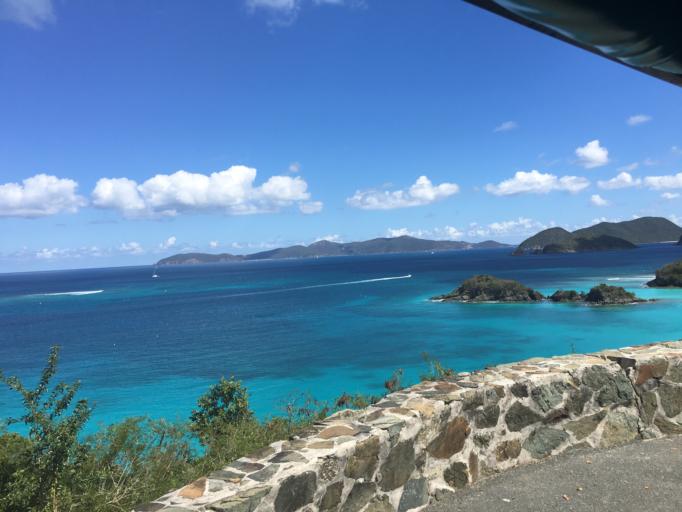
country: VI
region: Saint John Island
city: Cruz Bay
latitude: 18.3510
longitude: -64.7710
